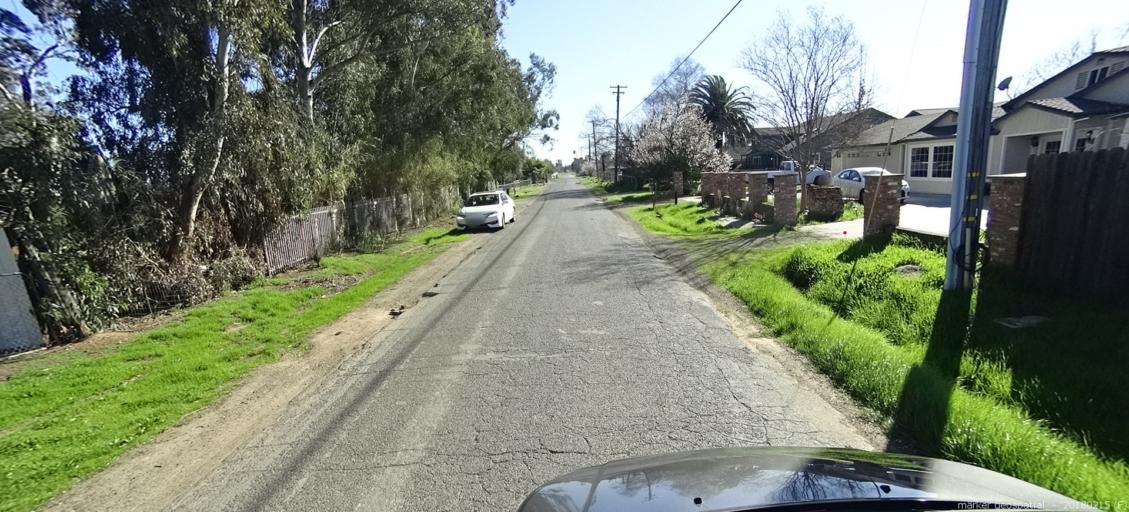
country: US
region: California
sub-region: Sacramento County
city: Rio Linda
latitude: 38.6804
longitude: -121.4615
